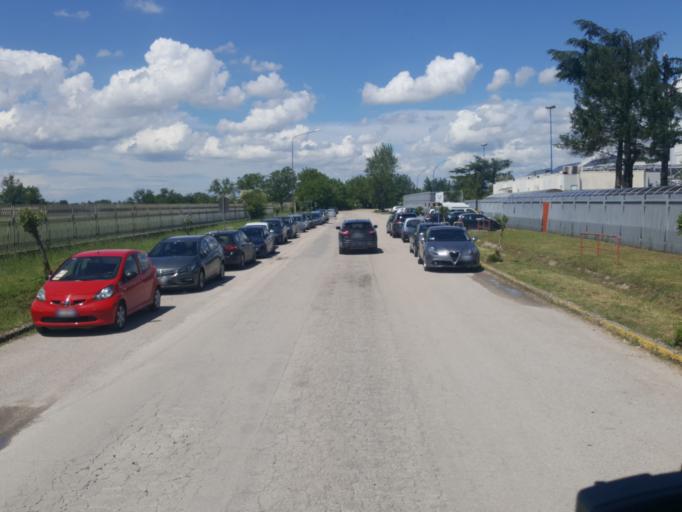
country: IT
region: Campania
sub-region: Provincia di Napoli
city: Pascarola
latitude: 40.9820
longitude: 14.2977
